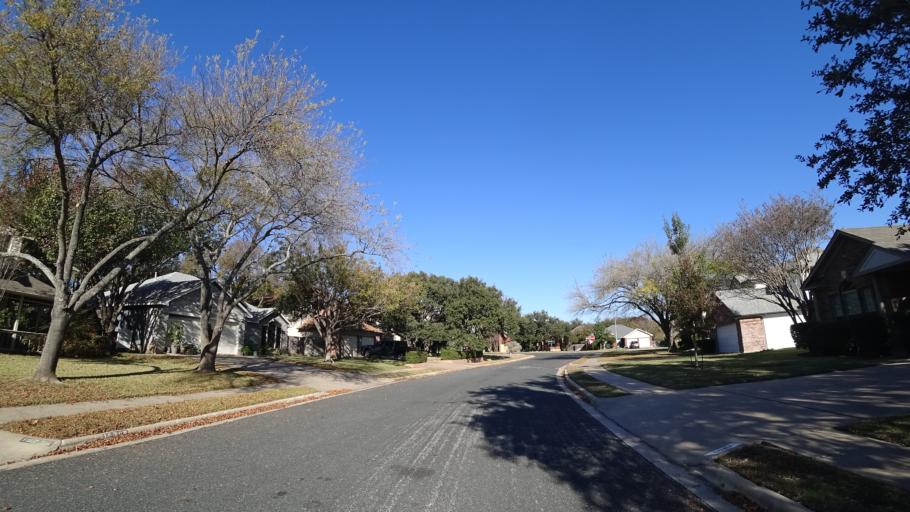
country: US
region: Texas
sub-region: Williamson County
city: Brushy Creek
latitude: 30.4891
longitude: -97.7385
